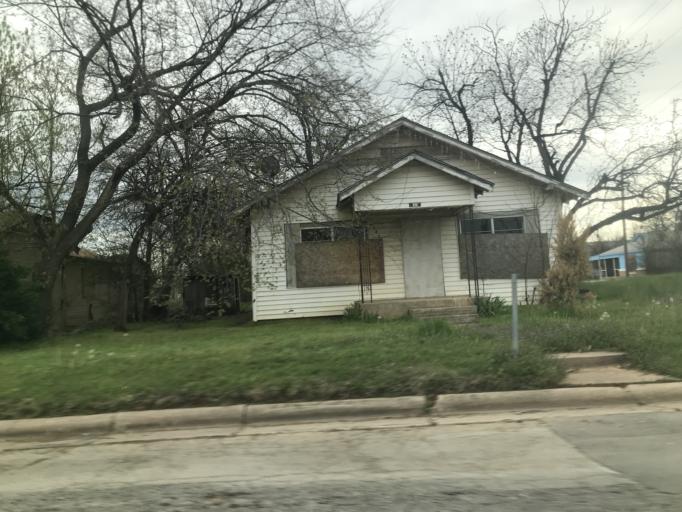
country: US
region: Texas
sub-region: Taylor County
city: Abilene
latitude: 32.4672
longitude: -99.7327
